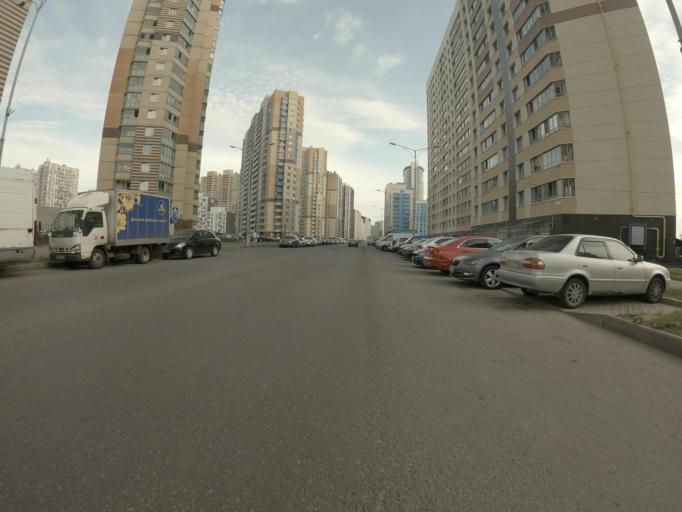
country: RU
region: Leningrad
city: Rybatskoye
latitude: 59.9062
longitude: 30.5127
